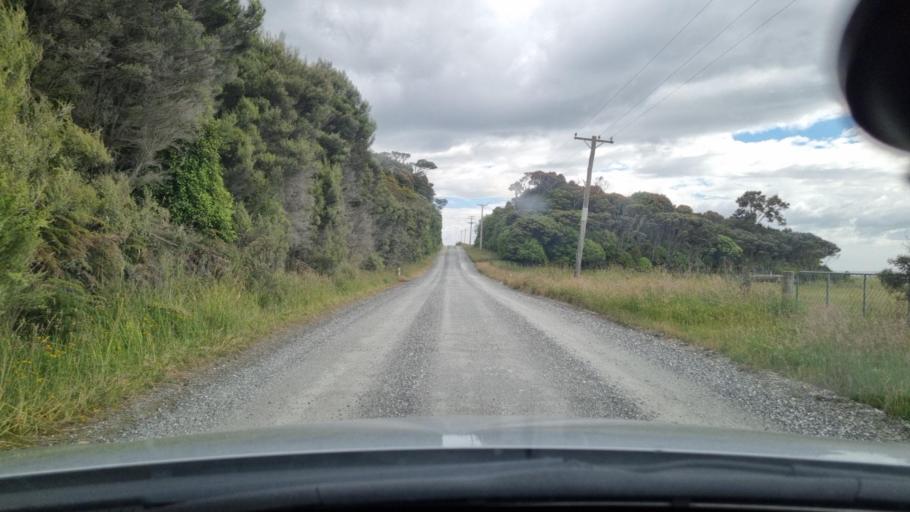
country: NZ
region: Southland
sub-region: Invercargill City
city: Bluff
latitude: -46.5289
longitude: 168.2689
